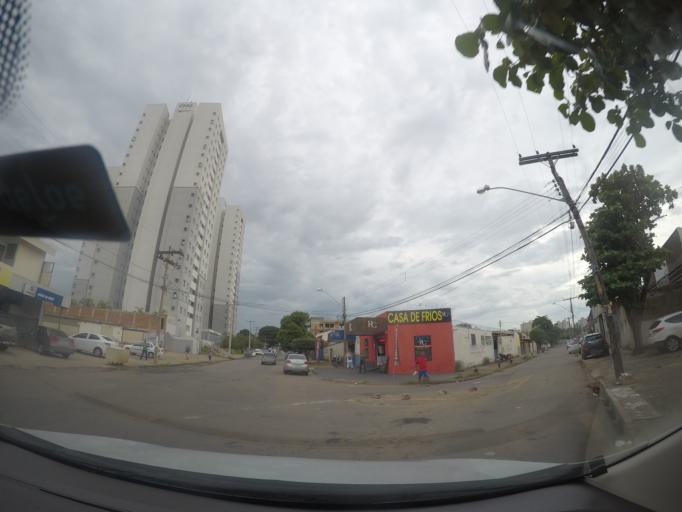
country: BR
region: Goias
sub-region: Goiania
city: Goiania
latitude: -16.6571
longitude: -49.2448
